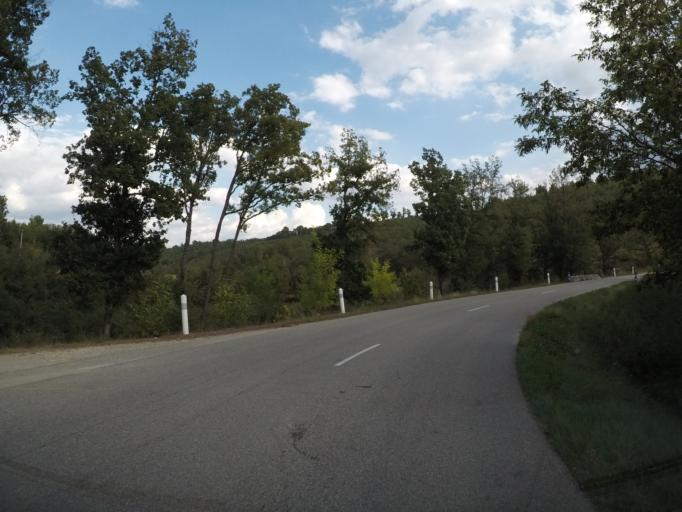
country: FR
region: Provence-Alpes-Cote d'Azur
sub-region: Departement des Alpes-de-Haute-Provence
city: Riez
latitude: 43.8299
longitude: 6.0439
